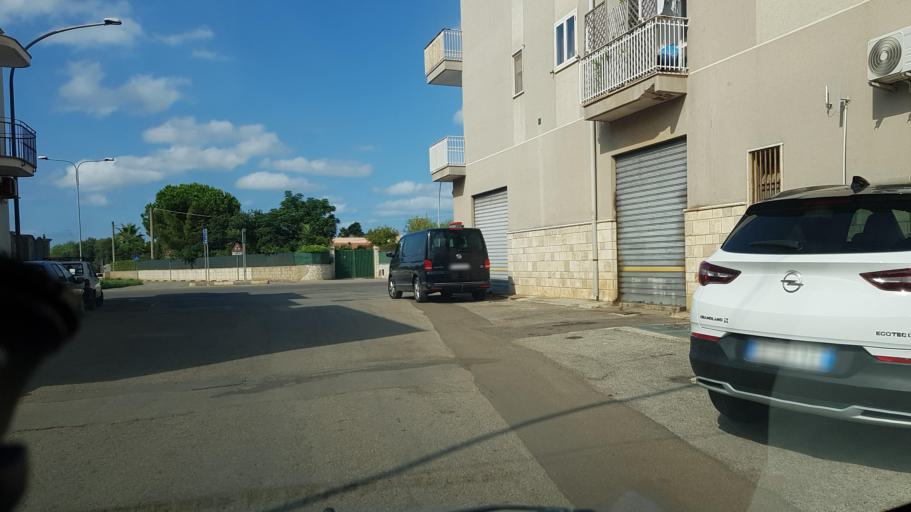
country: IT
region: Apulia
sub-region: Provincia di Brindisi
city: San Vito dei Normanni
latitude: 40.6573
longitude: 17.7180
